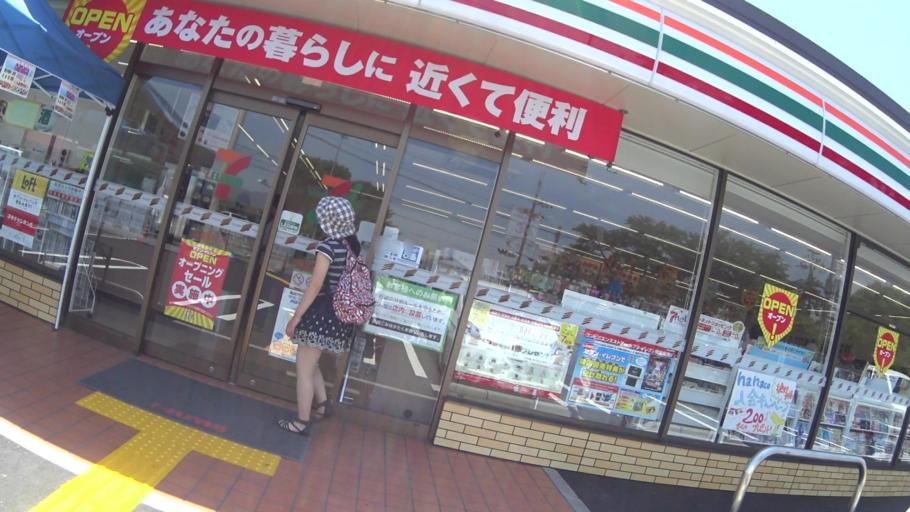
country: JP
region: Kyoto
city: Ayabe
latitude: 35.2597
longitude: 135.1957
